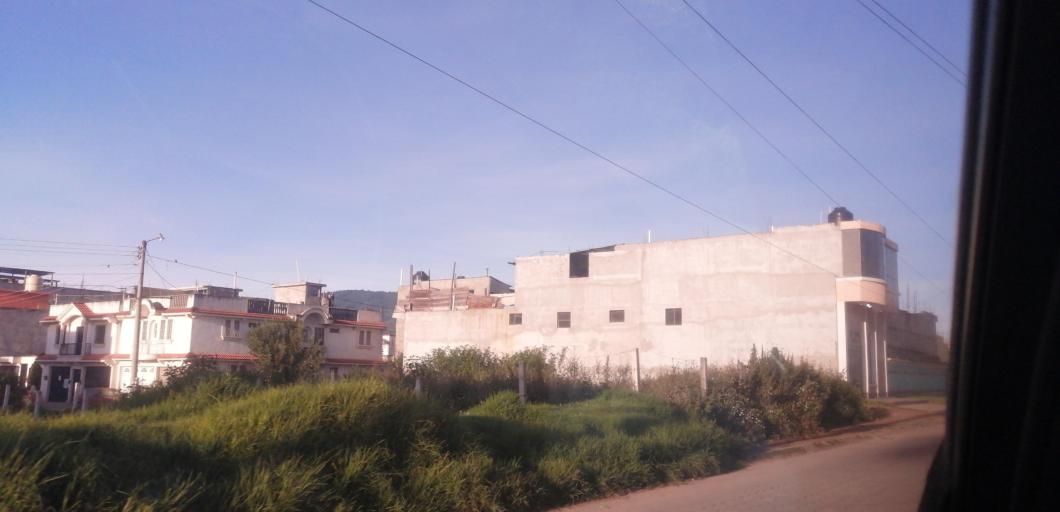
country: GT
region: Quetzaltenango
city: Olintepeque
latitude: 14.8667
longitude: -91.5226
